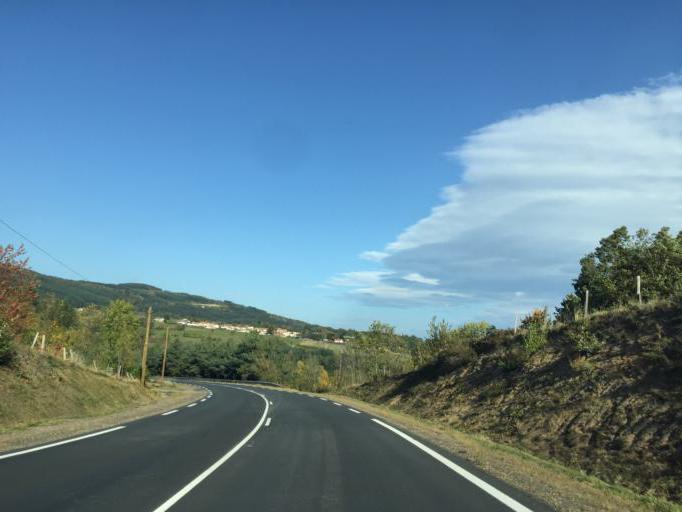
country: FR
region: Rhone-Alpes
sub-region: Departement de la Loire
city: Saint-Bonnet-le-Chateau
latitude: 45.4376
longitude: 4.0715
